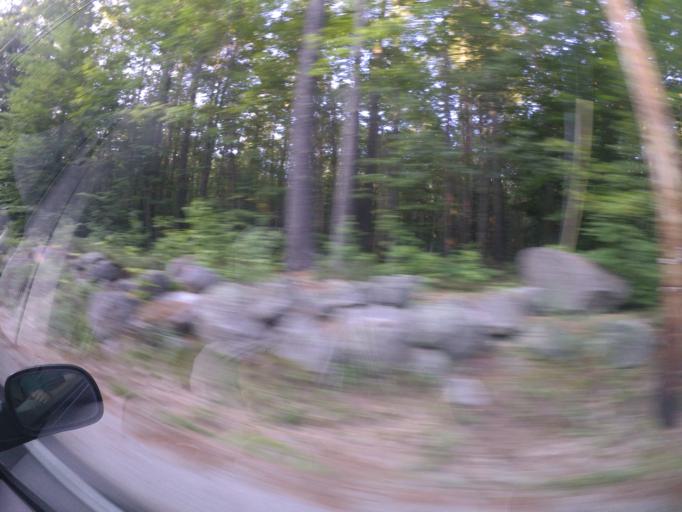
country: US
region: Maine
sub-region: Cumberland County
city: Raymond
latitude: 43.8935
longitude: -70.4406
